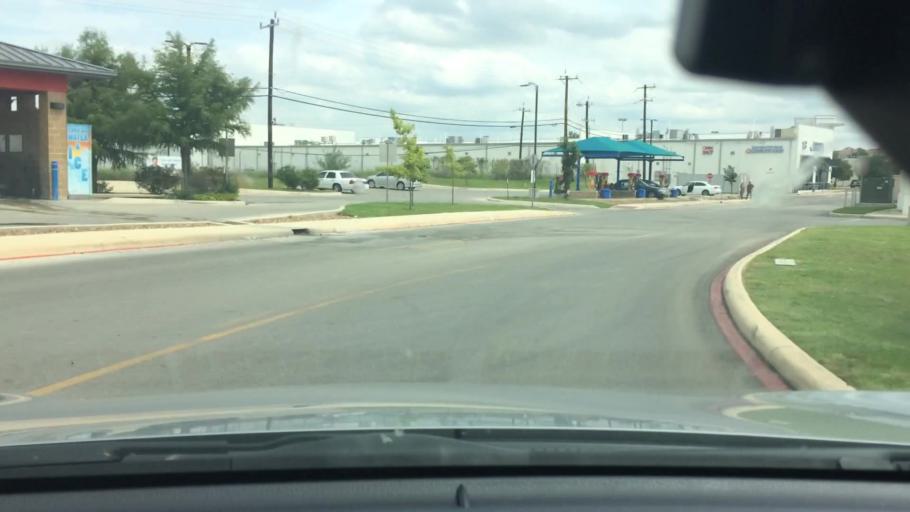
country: US
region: Texas
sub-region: Bexar County
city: San Antonio
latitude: 29.3527
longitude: -98.4528
